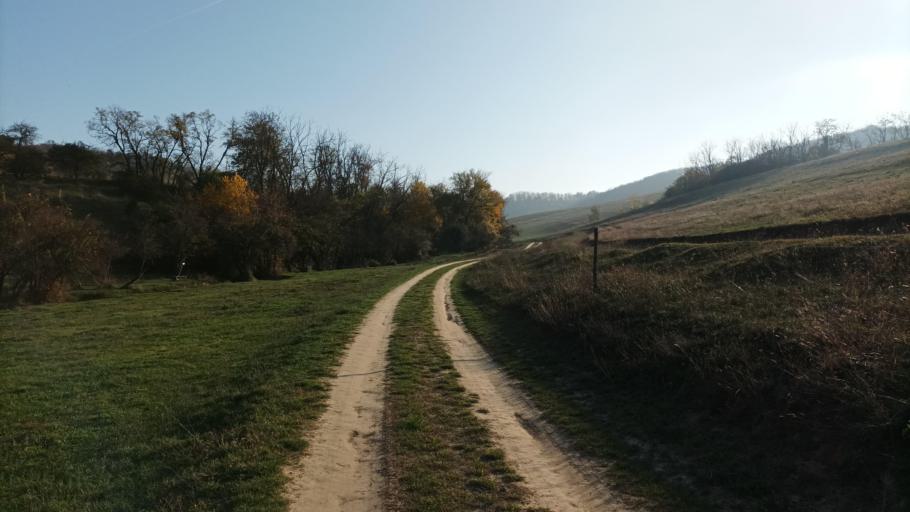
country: HU
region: Tolna
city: Szentgalpuszta
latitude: 46.3341
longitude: 18.6073
